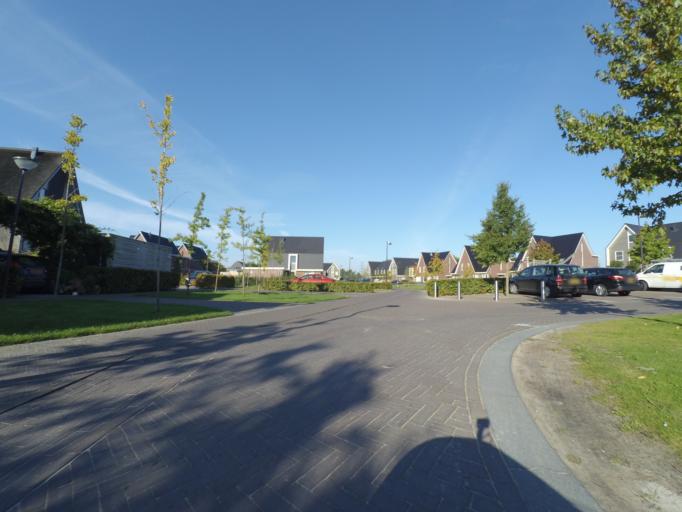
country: NL
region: Gelderland
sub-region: Gemeente Putten
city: Putten
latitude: 52.2599
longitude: 5.5776
